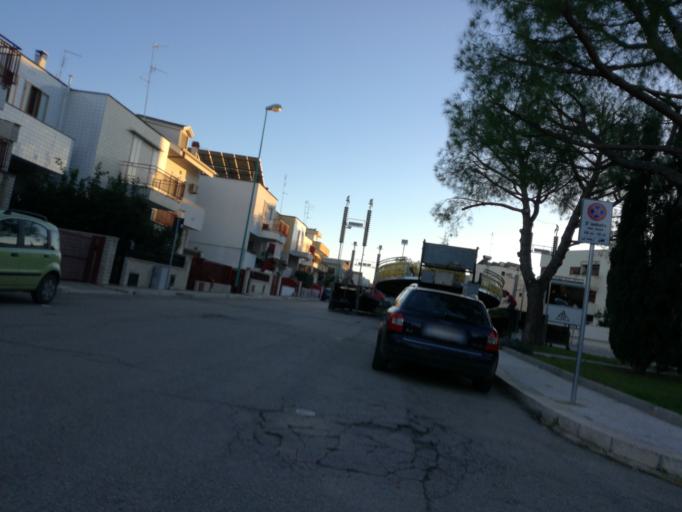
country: IT
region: Apulia
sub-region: Provincia di Bari
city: Adelfia
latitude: 41.0013
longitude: 16.8803
